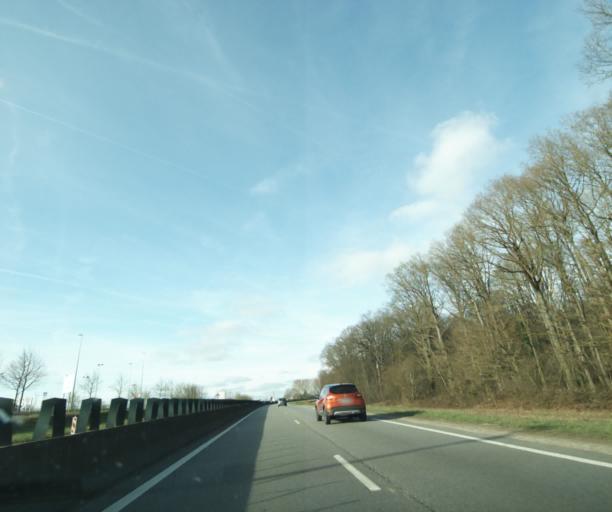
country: FR
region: Ile-de-France
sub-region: Departement des Yvelines
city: Rambouillet
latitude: 48.6246
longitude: 1.8306
